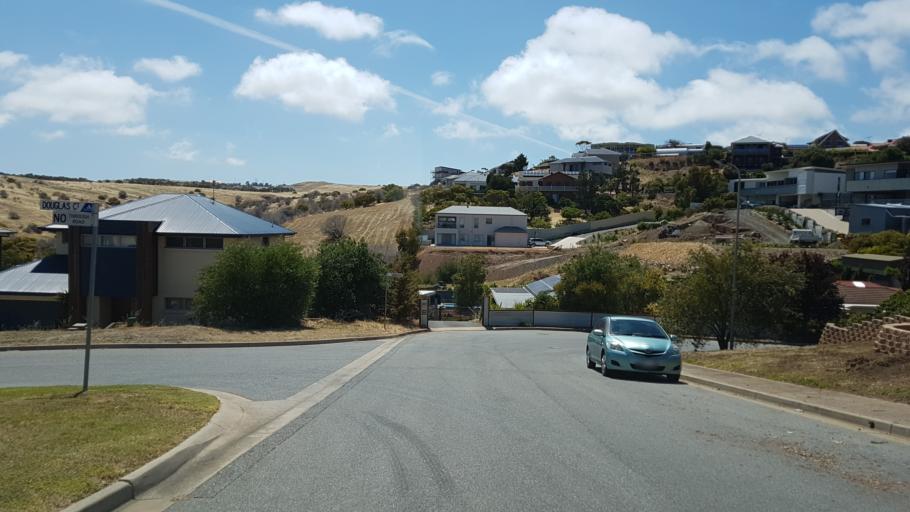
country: AU
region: South Australia
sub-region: Marion
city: Marino
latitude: -35.0628
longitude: 138.5093
